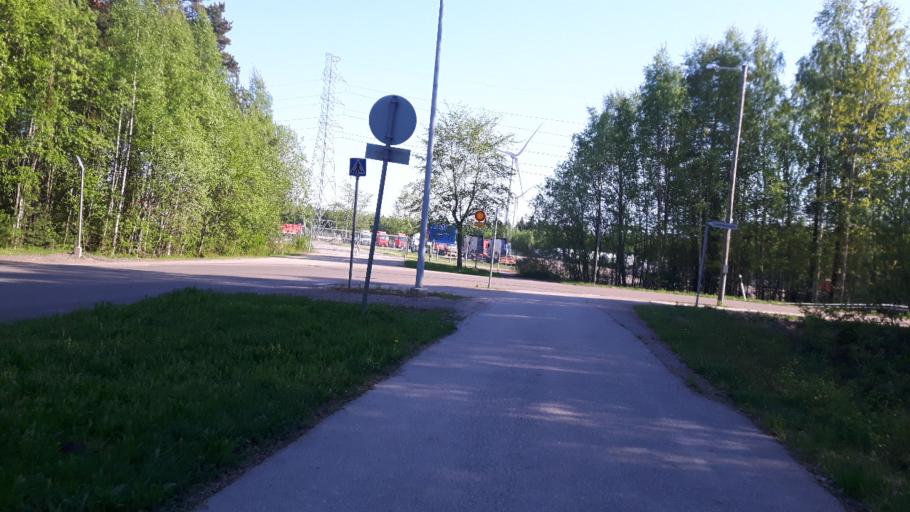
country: FI
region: Kymenlaakso
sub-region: Kotka-Hamina
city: Kotka
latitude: 60.4362
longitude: 26.8814
